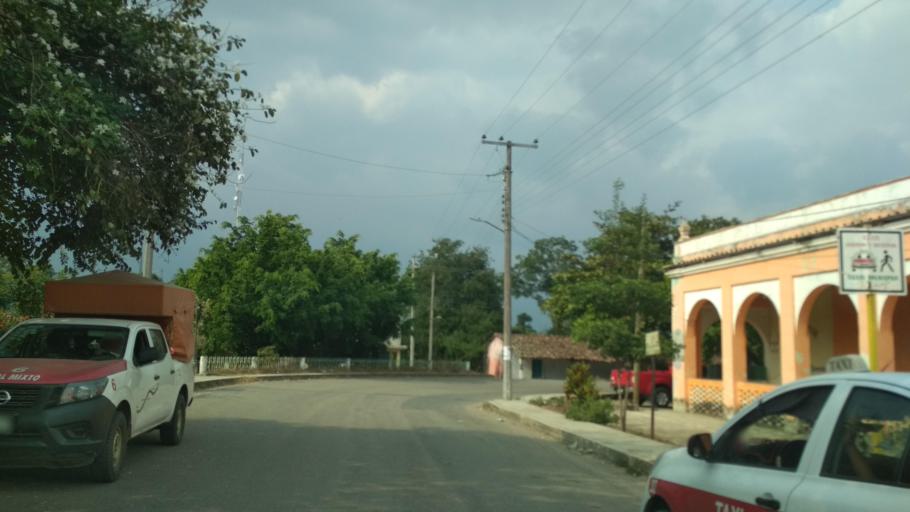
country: MM
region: Kayah
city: Loikaw
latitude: 20.2383
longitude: 97.2768
